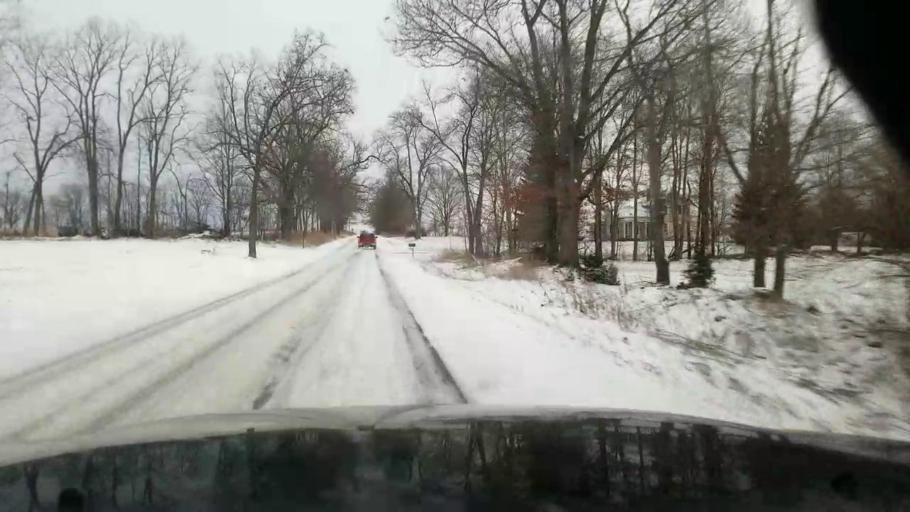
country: US
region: Michigan
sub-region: Jackson County
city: Spring Arbor
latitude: 42.1533
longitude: -84.4993
